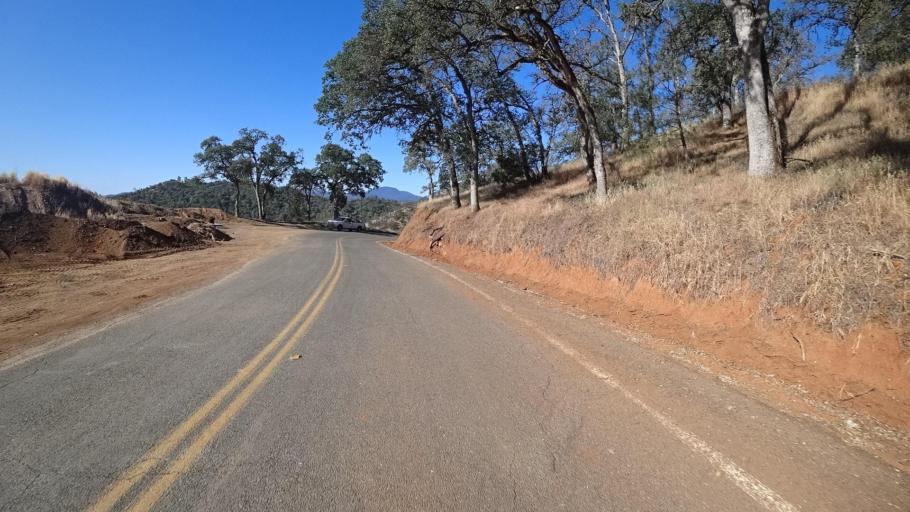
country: US
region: California
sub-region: Lake County
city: Clearlake Oaks
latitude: 38.9943
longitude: -122.6823
